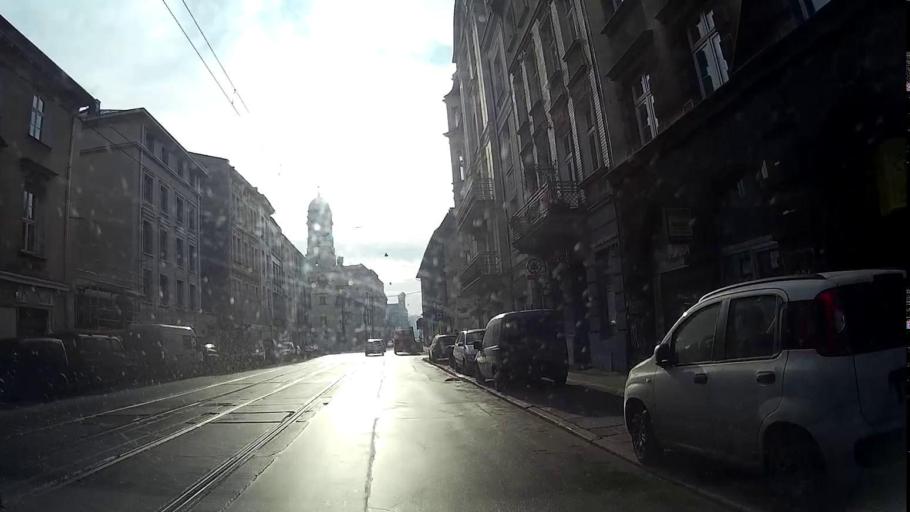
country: PL
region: Lesser Poland Voivodeship
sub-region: Krakow
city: Krakow
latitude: 50.0498
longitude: 19.9429
